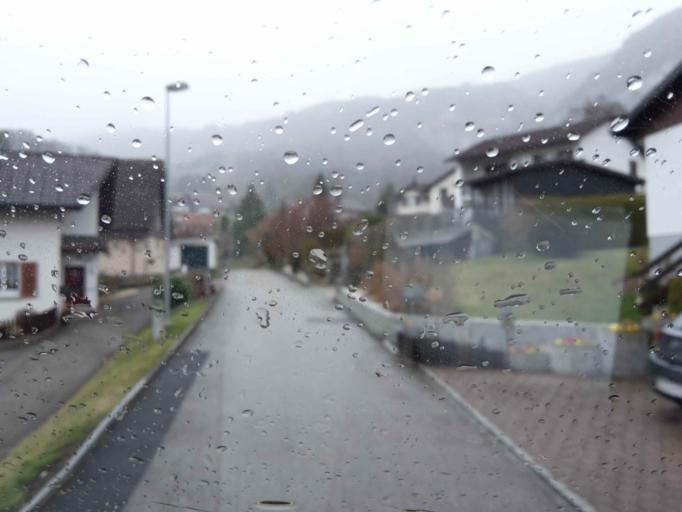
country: CH
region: Solothurn
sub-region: Bezirk Thal
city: Welschenrohr
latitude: 47.2820
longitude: 7.5237
